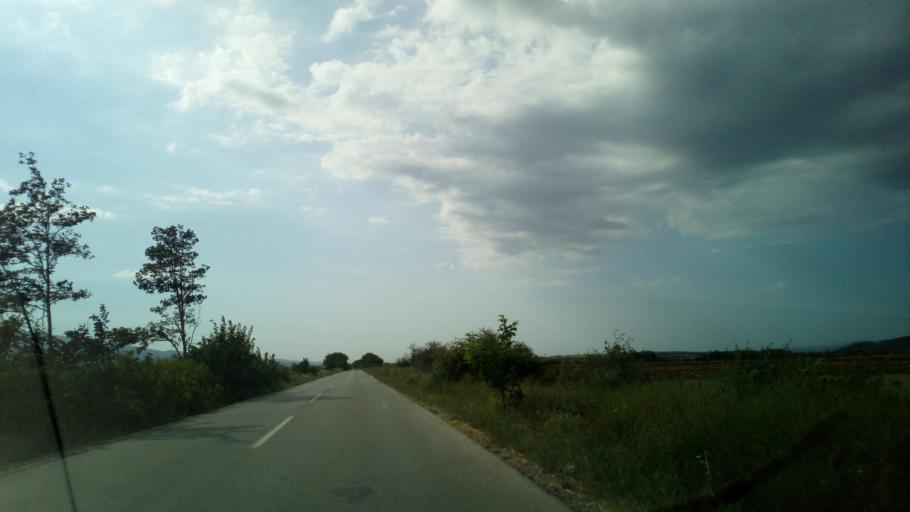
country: GR
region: Central Macedonia
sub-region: Nomos Thessalonikis
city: Gerakarou
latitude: 40.5795
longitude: 23.2695
